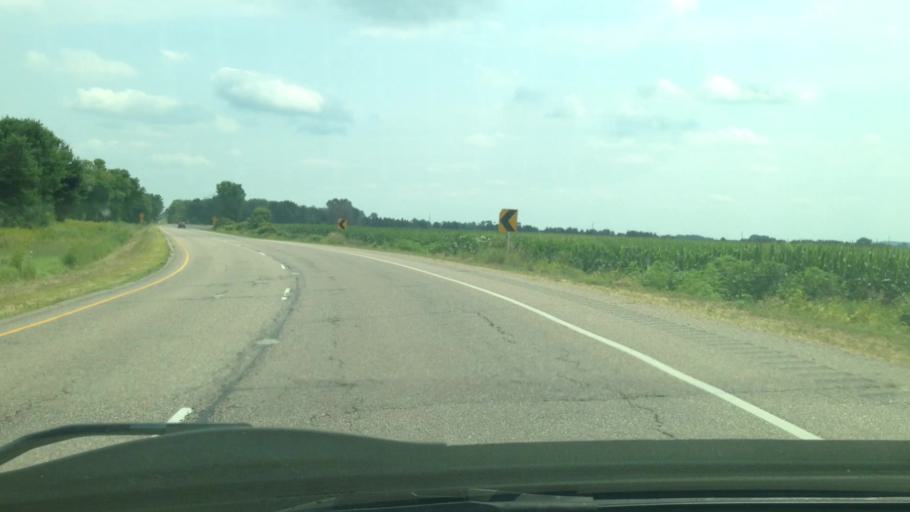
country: US
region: Wisconsin
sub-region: Sauk County
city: Prairie du Sac
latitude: 43.3511
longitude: -89.7659
